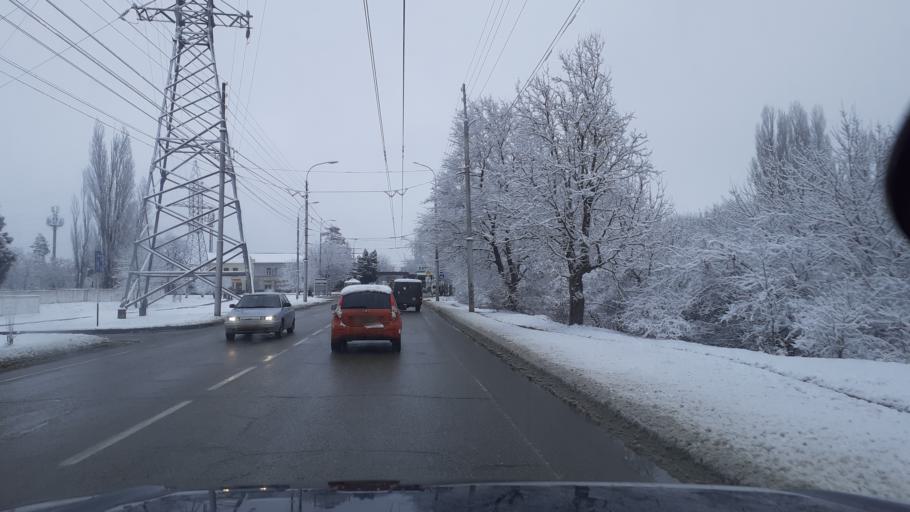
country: RU
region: Adygeya
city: Maykop
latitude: 44.5909
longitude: 40.1184
